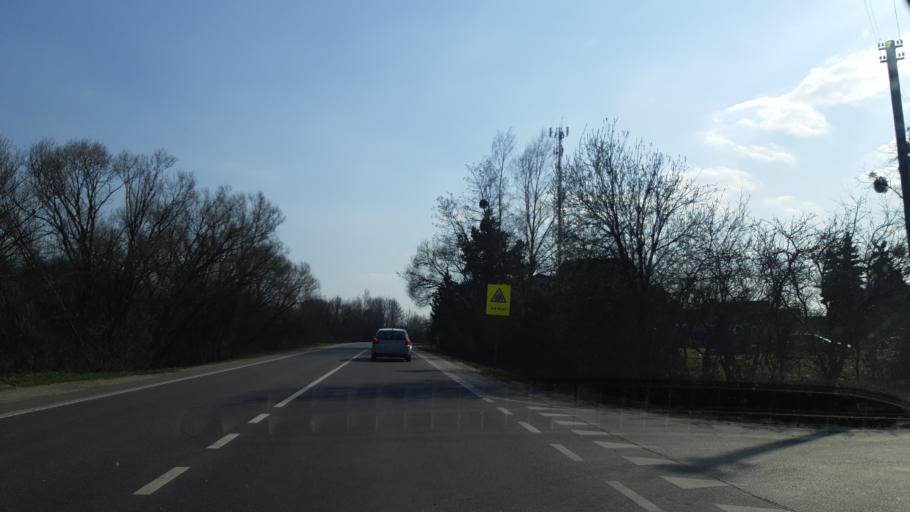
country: LT
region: Kauno apskritis
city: Dainava (Kaunas)
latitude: 54.8639
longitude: 23.9861
